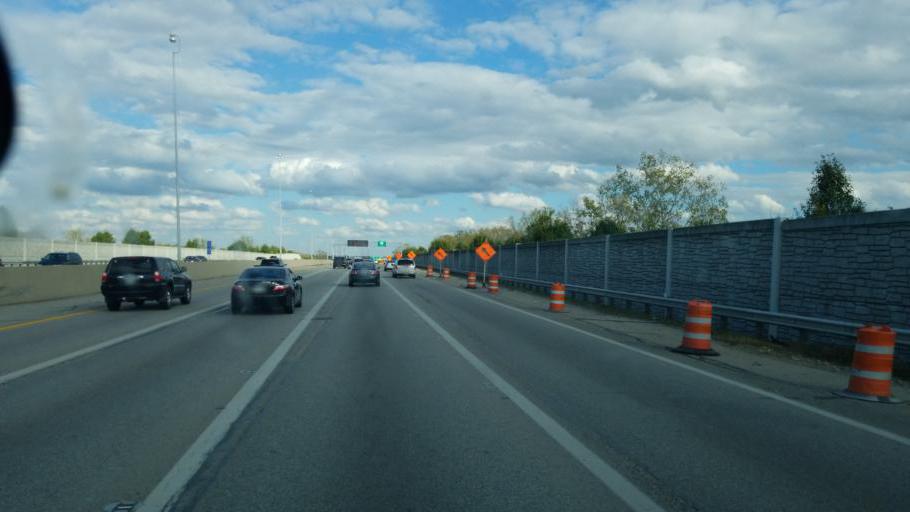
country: US
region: Ohio
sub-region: Franklin County
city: Worthington
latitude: 40.1108
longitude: -83.0622
